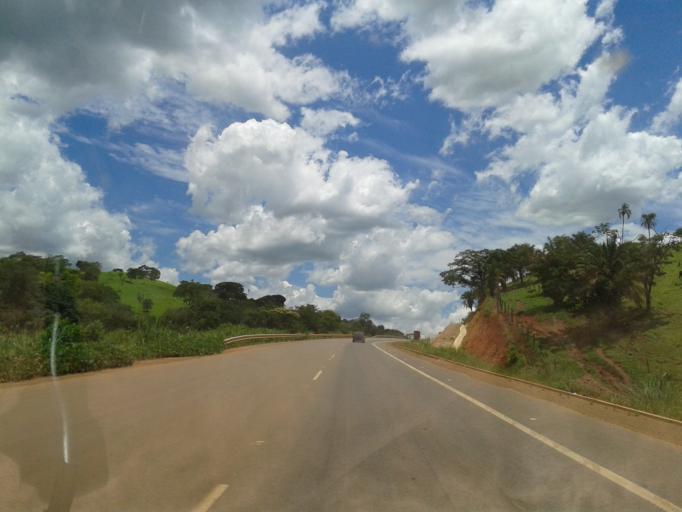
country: BR
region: Goias
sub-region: Petrolina De Goias
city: Petrolina de Goias
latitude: -16.2209
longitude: -49.3057
